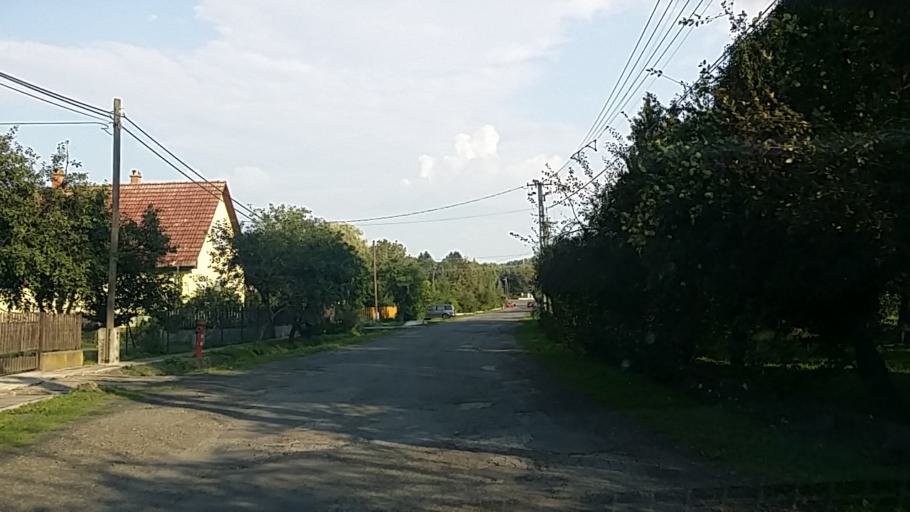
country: HU
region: Nograd
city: Bujak
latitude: 47.8644
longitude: 19.5044
